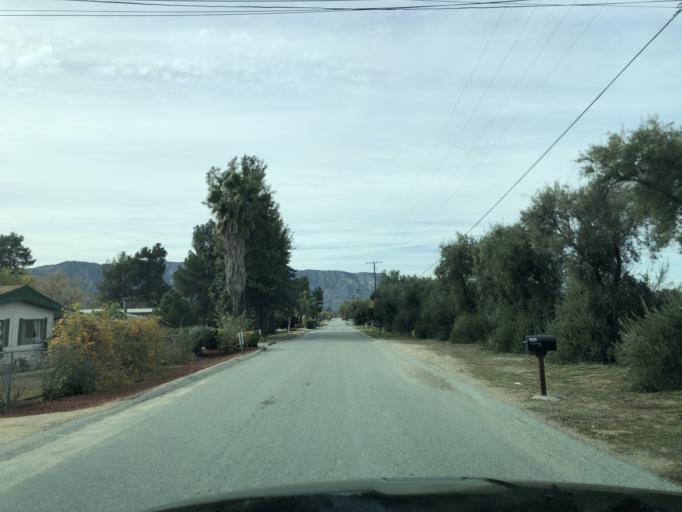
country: US
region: California
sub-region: Riverside County
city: Wildomar
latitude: 33.6159
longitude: -117.2716
